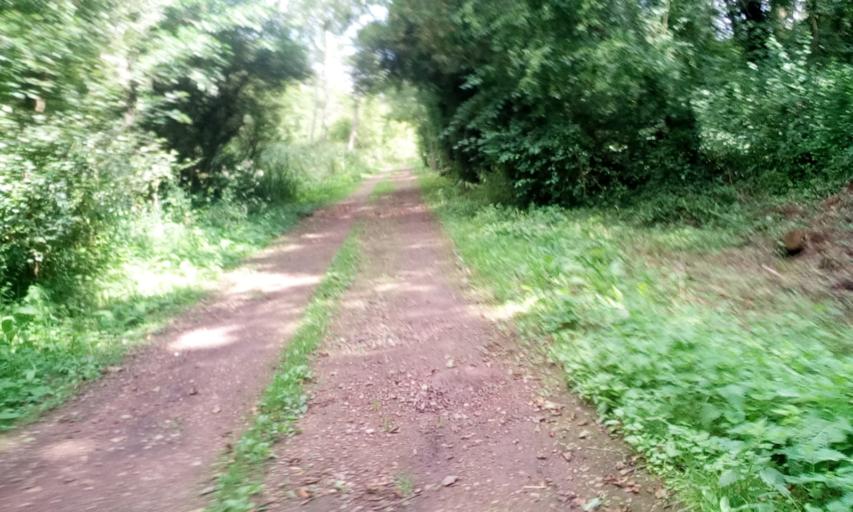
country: FR
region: Lower Normandy
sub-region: Departement du Calvados
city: Bellengreville
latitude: 49.1143
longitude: -0.2191
